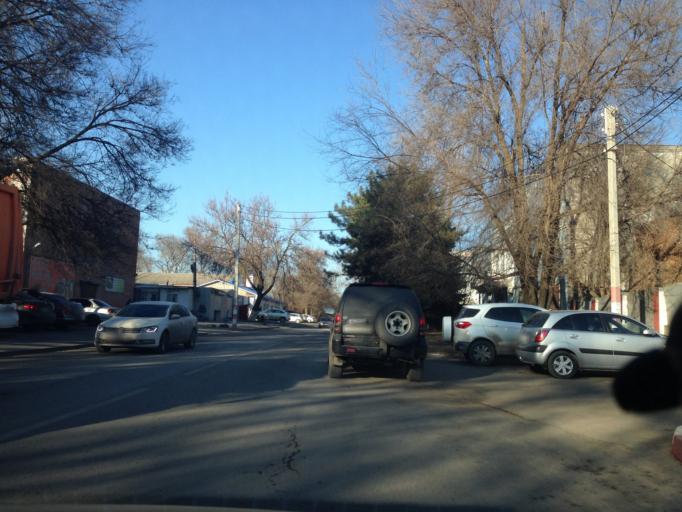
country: RU
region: Rostov
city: Rostov-na-Donu
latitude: 47.2378
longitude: 39.7190
